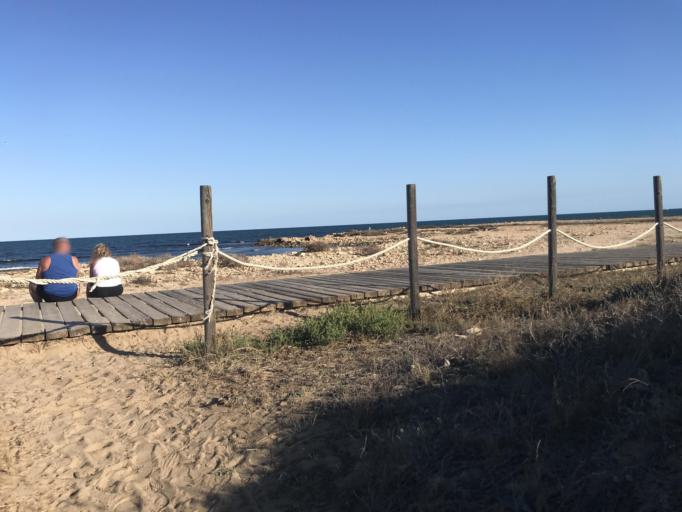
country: ES
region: Valencia
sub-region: Provincia de Alicante
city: Torrevieja
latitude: 38.0301
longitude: -0.6514
